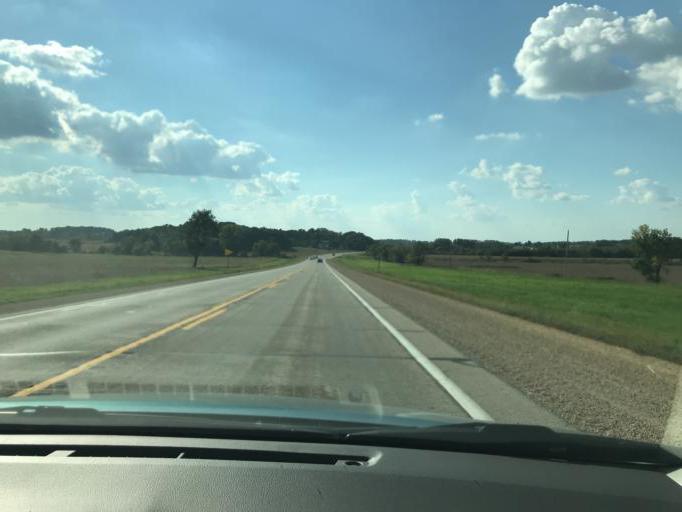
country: US
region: Wisconsin
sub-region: Green County
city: Brodhead
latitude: 42.5886
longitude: -89.4785
